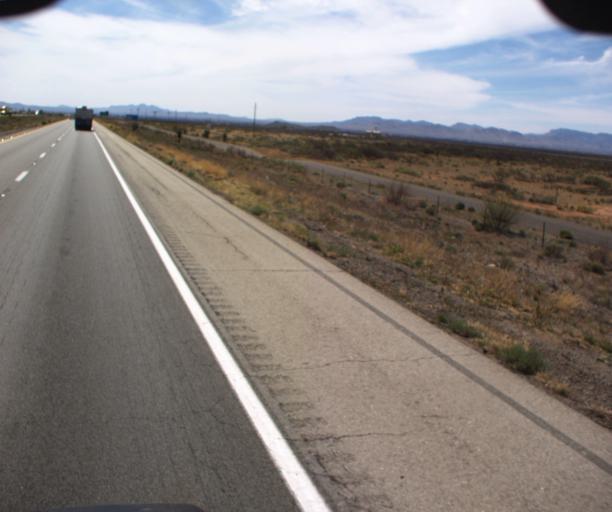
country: US
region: Arizona
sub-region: Cochise County
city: Willcox
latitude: 32.3219
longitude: -109.7792
